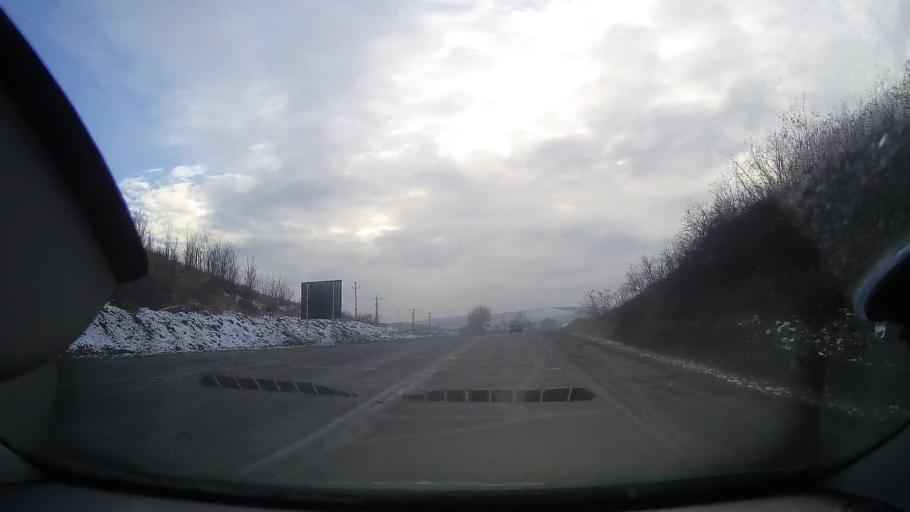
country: RO
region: Mures
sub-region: Comuna Iernut
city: Iernut
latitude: 46.4282
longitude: 24.2604
